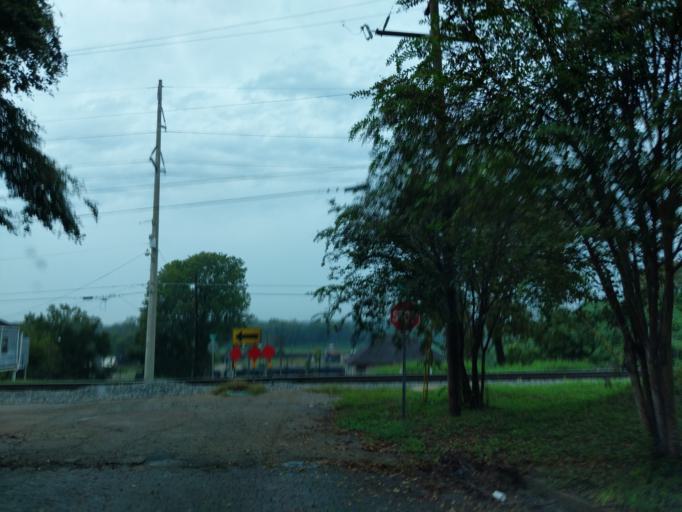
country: US
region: Mississippi
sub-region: Warren County
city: Vicksburg
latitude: 32.3417
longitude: -90.8866
